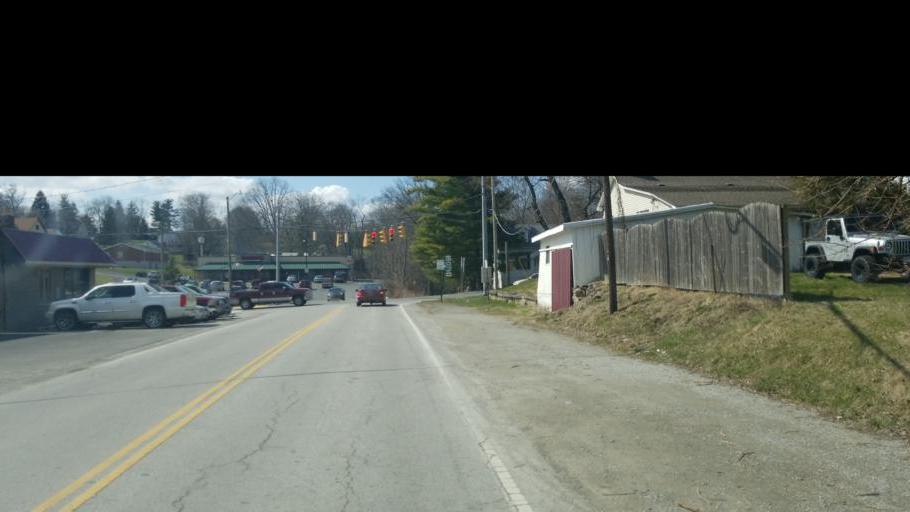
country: US
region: Ohio
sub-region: Highland County
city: Hillsboro
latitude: 39.1970
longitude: -83.6124
